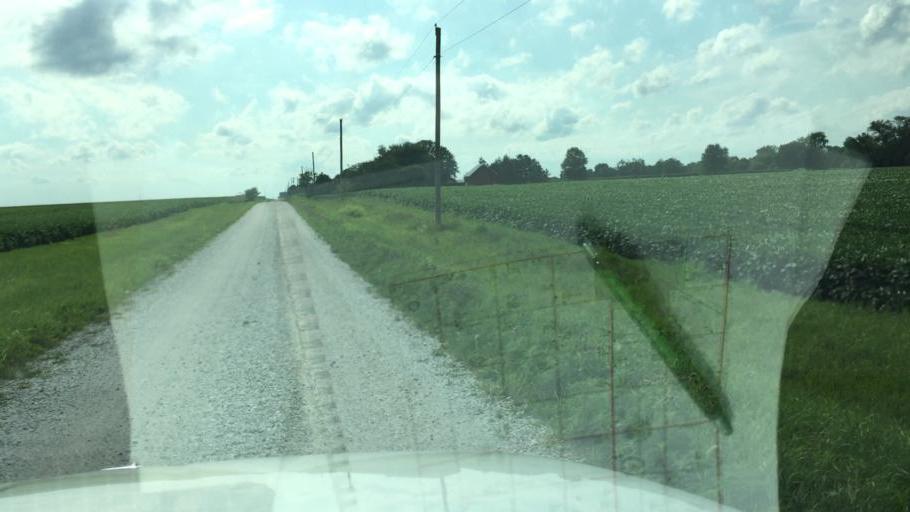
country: US
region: Illinois
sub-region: Hancock County
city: Carthage
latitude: 40.5356
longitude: -91.1684
